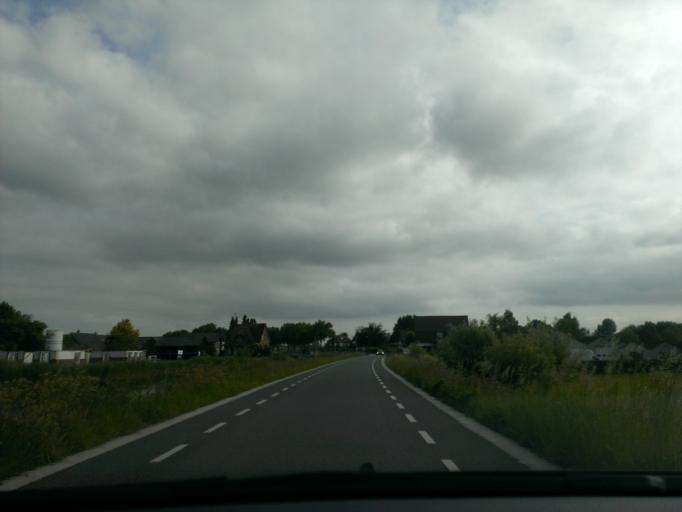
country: NL
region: Gelderland
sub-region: Gemeente Heerde
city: Heerde
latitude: 52.4227
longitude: 6.0783
